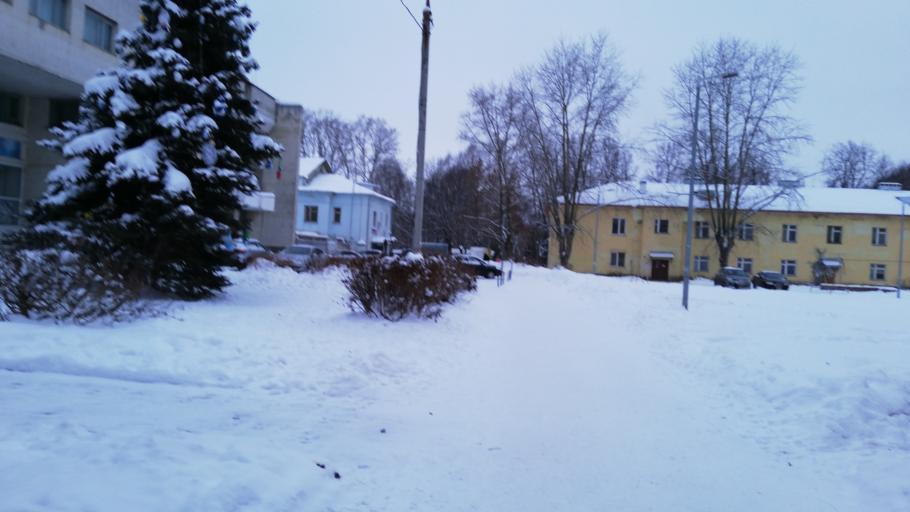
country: RU
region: Jaroslavl
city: Yaroslavl
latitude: 57.5756
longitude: 39.9244
